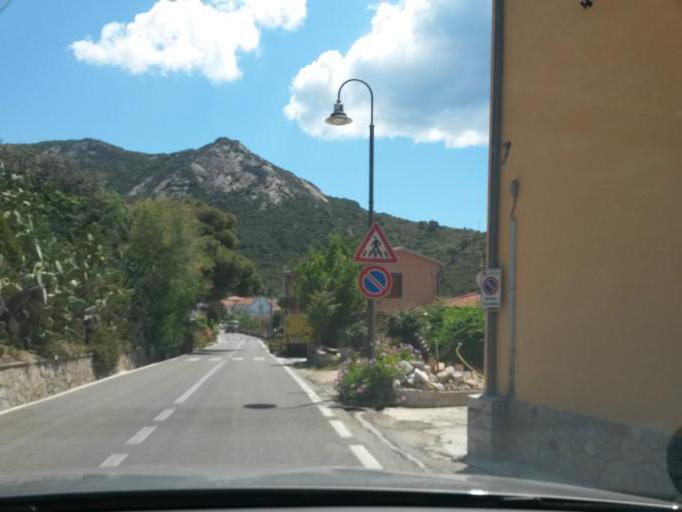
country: IT
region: Tuscany
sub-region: Provincia di Livorno
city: Marciana
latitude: 42.7496
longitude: 10.1193
